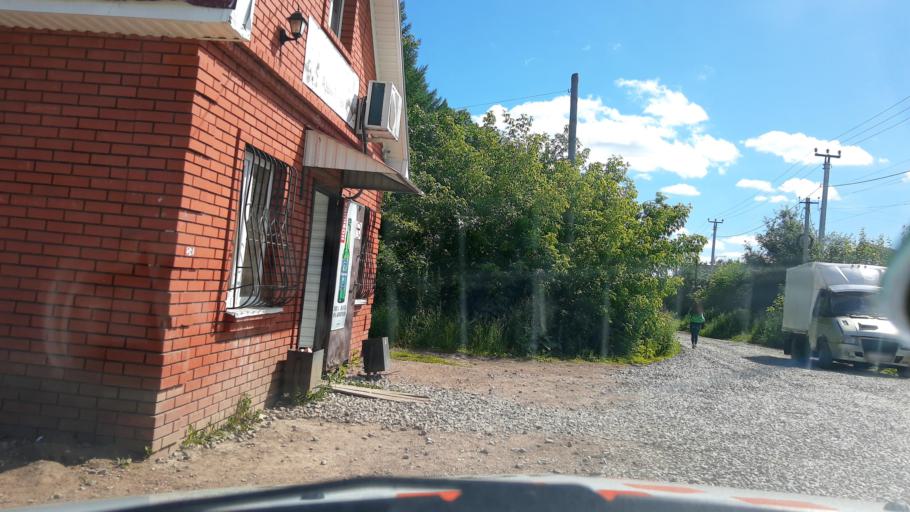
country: RU
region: Bashkortostan
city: Iglino
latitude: 54.8433
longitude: 56.4231
